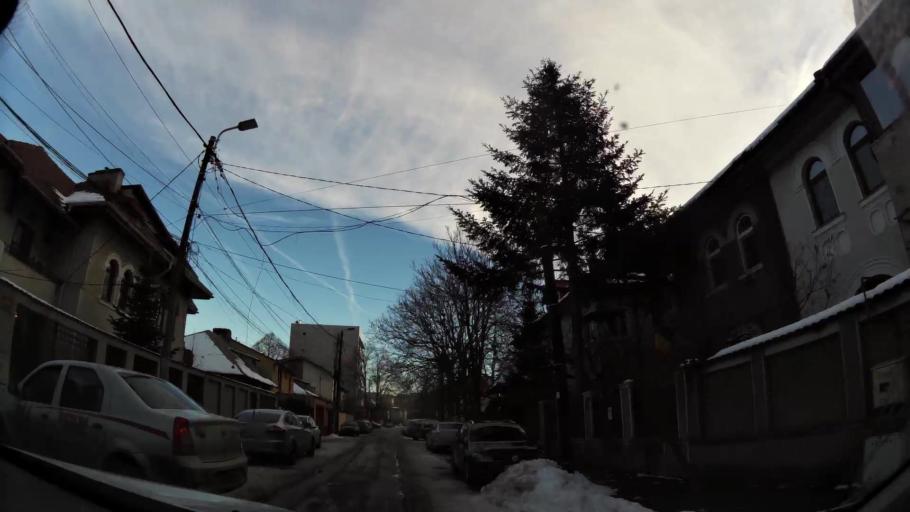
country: RO
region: Bucuresti
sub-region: Municipiul Bucuresti
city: Bucharest
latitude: 44.4260
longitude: 26.1309
